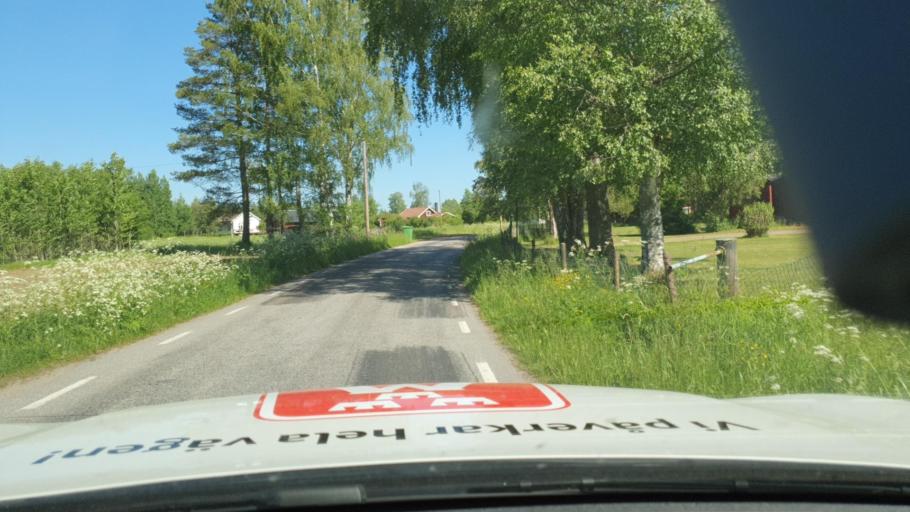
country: SE
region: Vaestra Goetaland
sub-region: Skovde Kommun
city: Skultorp
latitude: 58.3295
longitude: 13.9329
